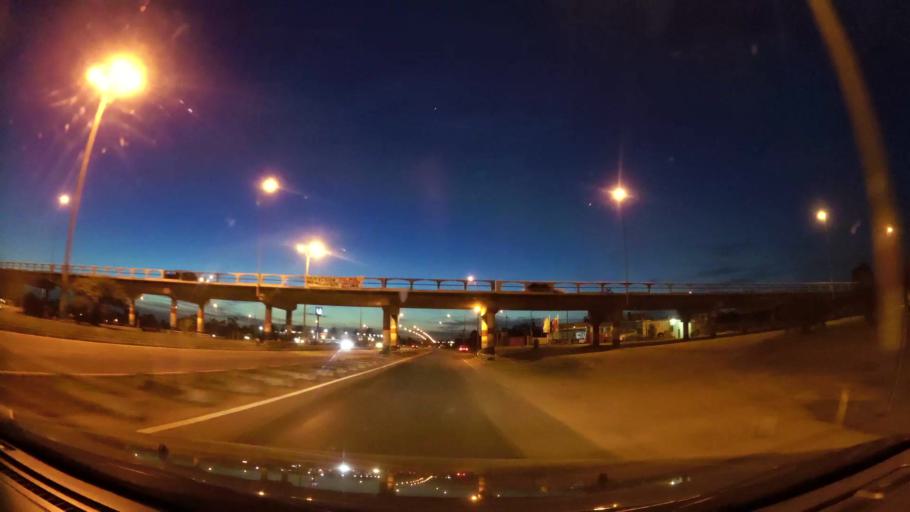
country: UY
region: Canelones
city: Atlantida
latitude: -34.7665
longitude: -55.7638
